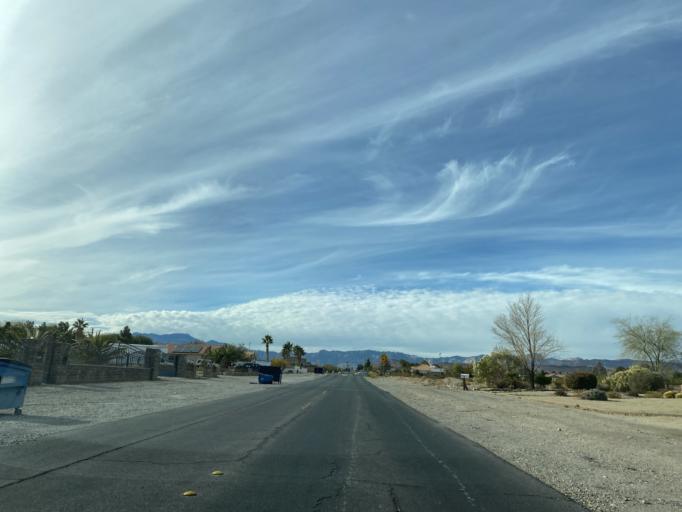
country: US
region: Nevada
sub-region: Clark County
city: Enterprise
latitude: 36.0338
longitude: -115.2586
